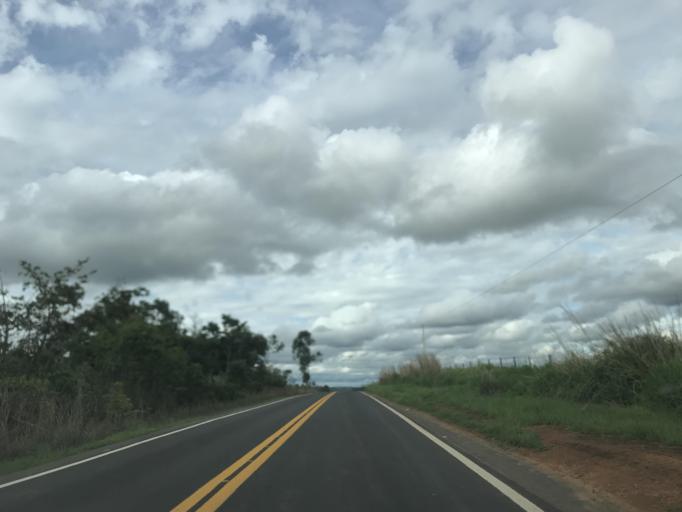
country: BR
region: Goias
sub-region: Bela Vista De Goias
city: Bela Vista de Goias
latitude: -17.1897
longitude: -48.6943
